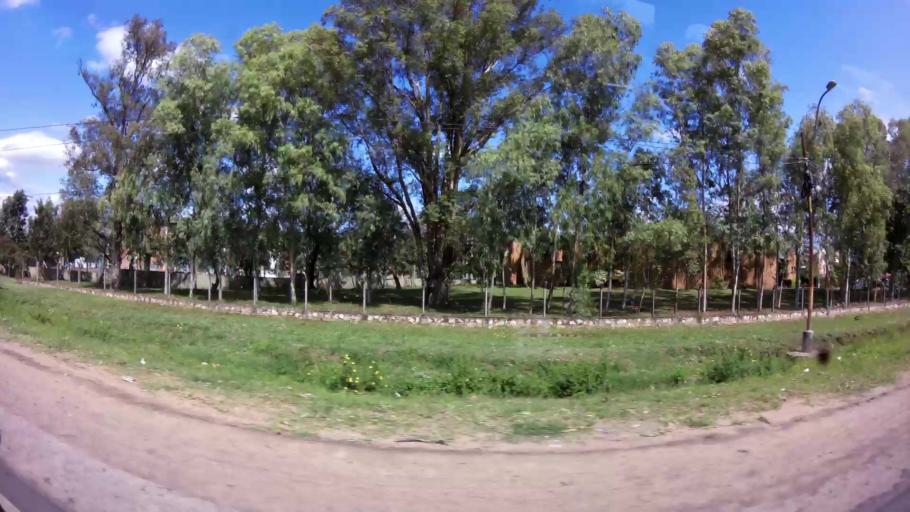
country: PY
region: Central
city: Fernando de la Mora
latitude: -25.2661
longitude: -57.5223
